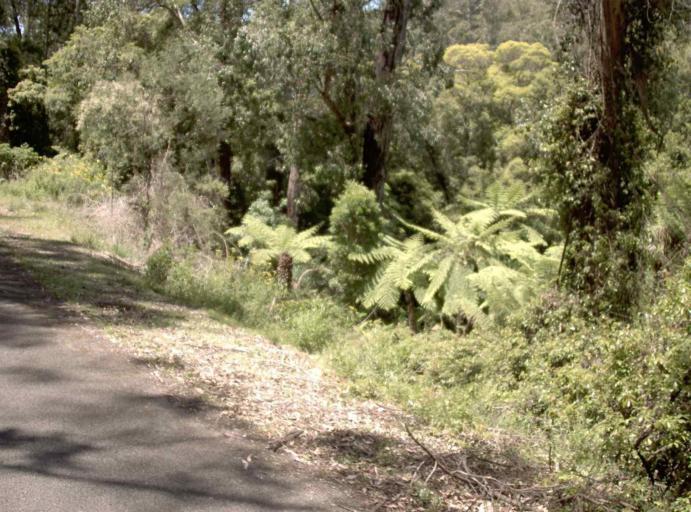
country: AU
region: New South Wales
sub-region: Bombala
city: Bombala
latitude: -37.4715
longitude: 148.9286
